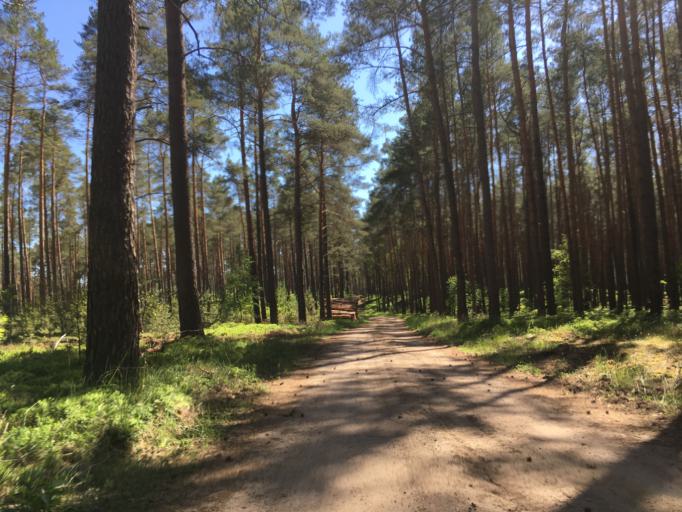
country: DE
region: Brandenburg
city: Friedrichswalde
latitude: 52.9826
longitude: 13.6277
